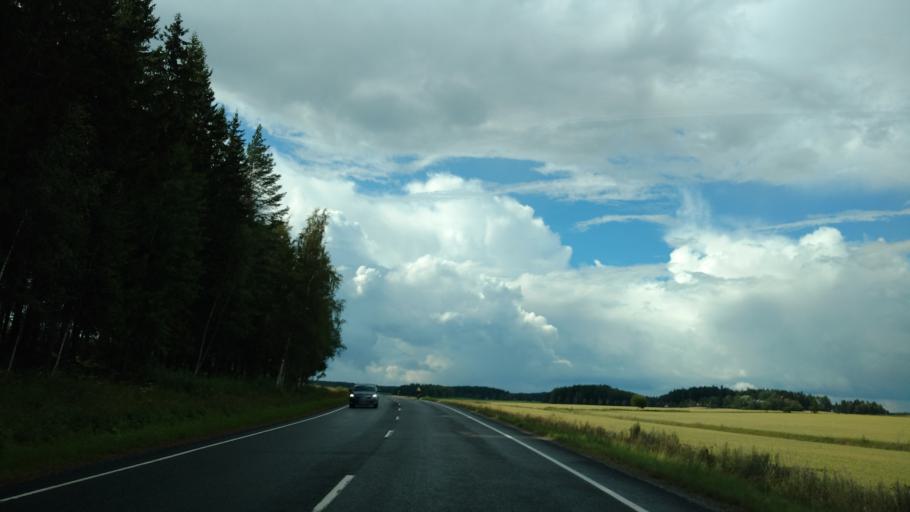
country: FI
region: Varsinais-Suomi
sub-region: Turku
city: Sauvo
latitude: 60.3884
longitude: 22.8780
